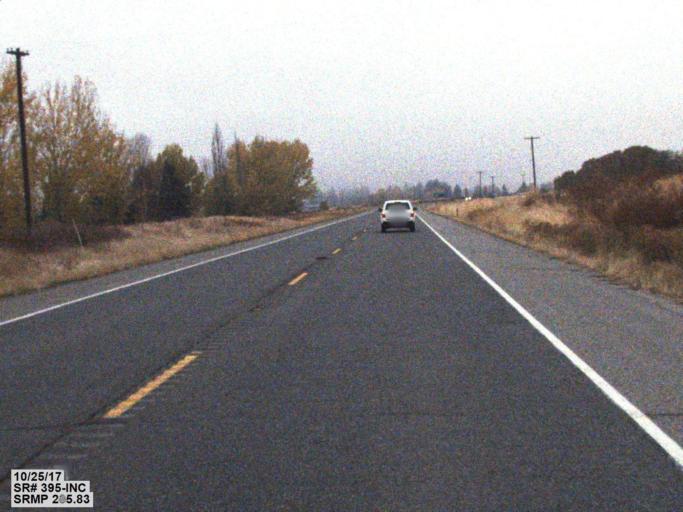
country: US
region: Washington
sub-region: Stevens County
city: Kettle Falls
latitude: 48.5983
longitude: -118.0106
